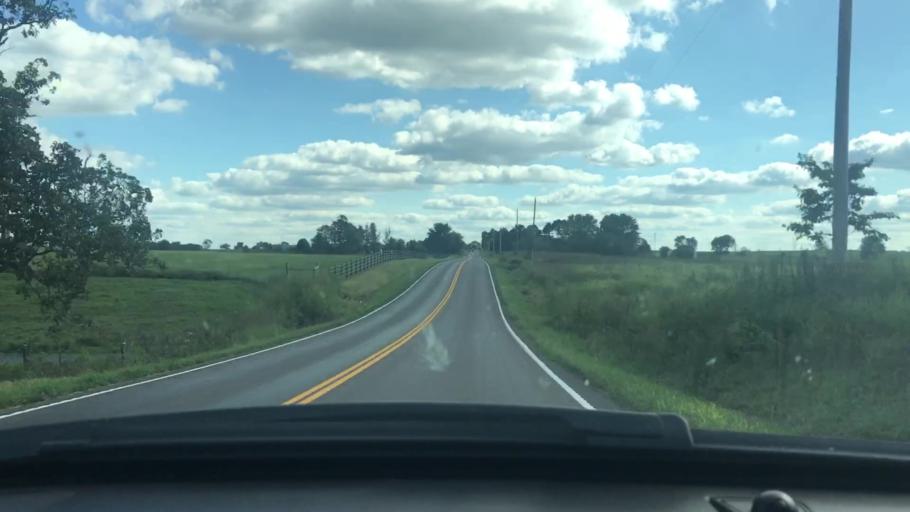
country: US
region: Missouri
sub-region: Wright County
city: Mountain Grove
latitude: 37.1746
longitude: -92.2670
